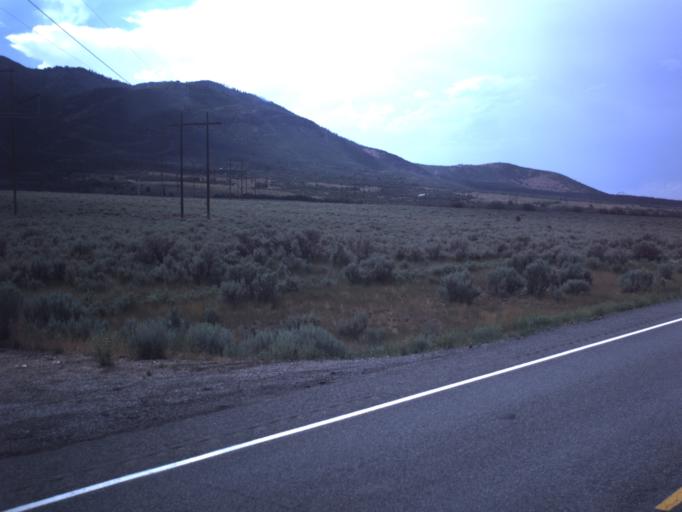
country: US
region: Utah
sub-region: Sanpete County
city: Fountain Green
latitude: 39.6923
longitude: -111.6878
